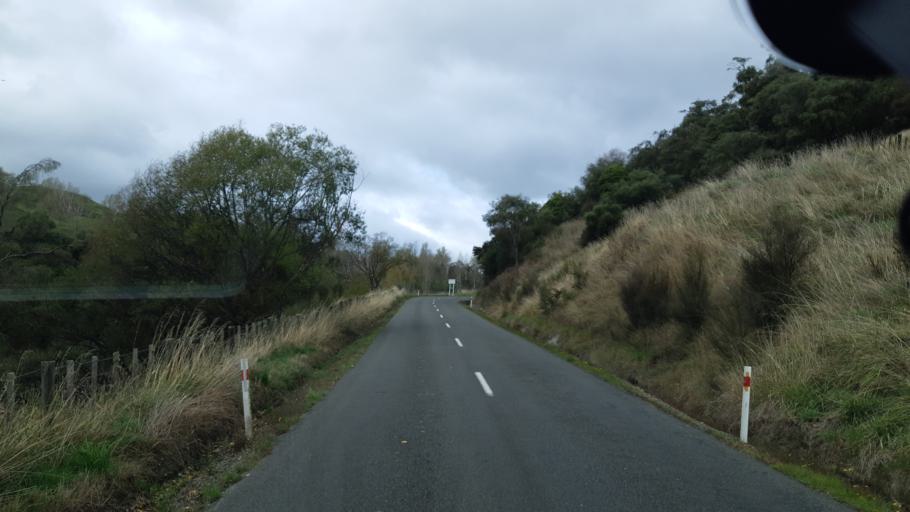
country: NZ
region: Manawatu-Wanganui
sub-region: Ruapehu District
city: Waiouru
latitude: -39.6513
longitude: 175.7269
